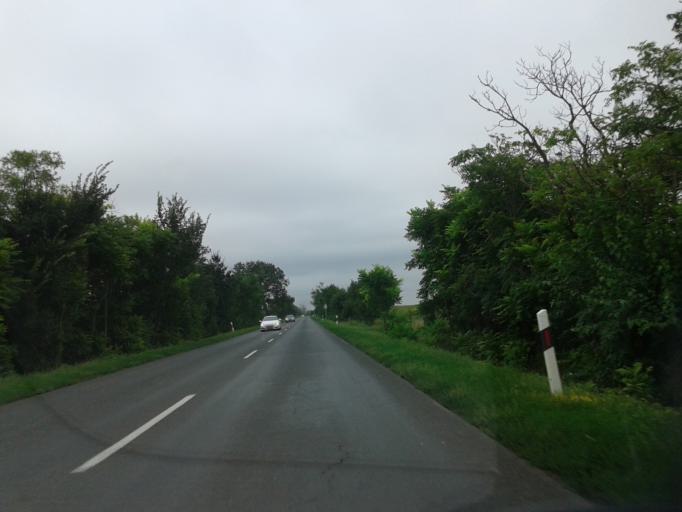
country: HU
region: Bacs-Kiskun
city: Solt
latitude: 46.7871
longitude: 19.0562
